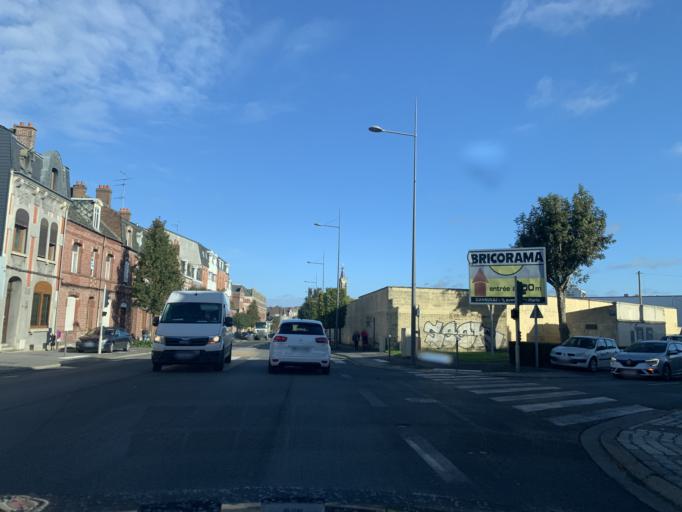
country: FR
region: Nord-Pas-de-Calais
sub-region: Departement du Nord
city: Cambrai
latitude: 50.1678
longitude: 3.2299
